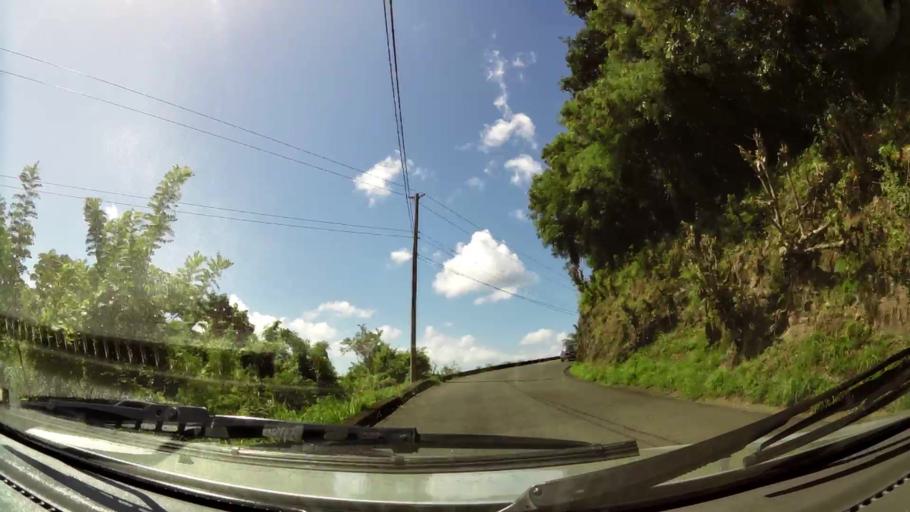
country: GD
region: Saint John
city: Gouyave
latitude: 12.1130
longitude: -61.7459
